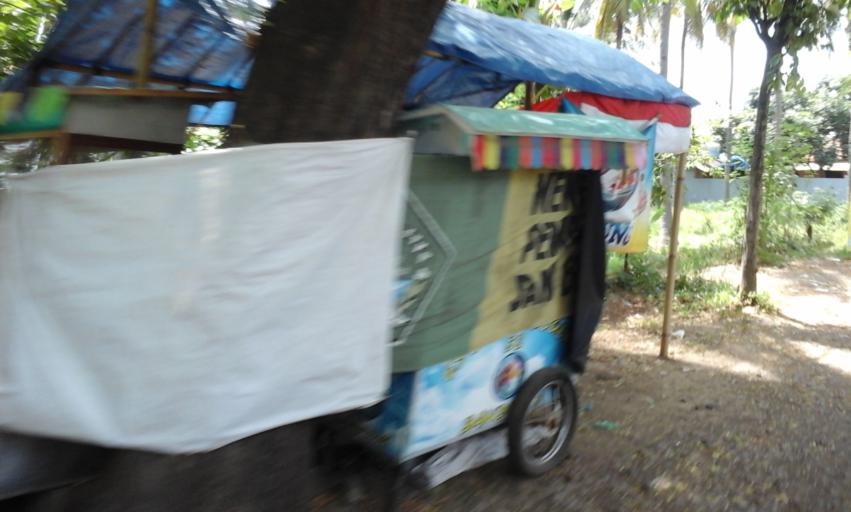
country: ID
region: East Java
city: Klatakan
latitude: -8.1658
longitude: 114.3884
